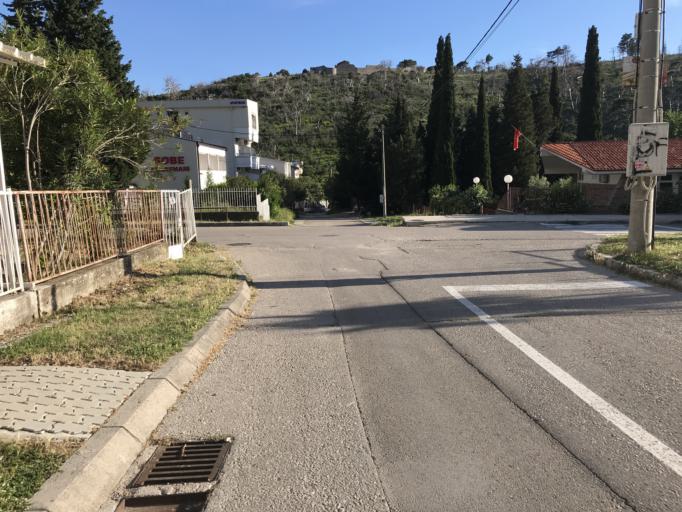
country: ME
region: Bar
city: Sutomore
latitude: 42.1403
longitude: 19.0454
